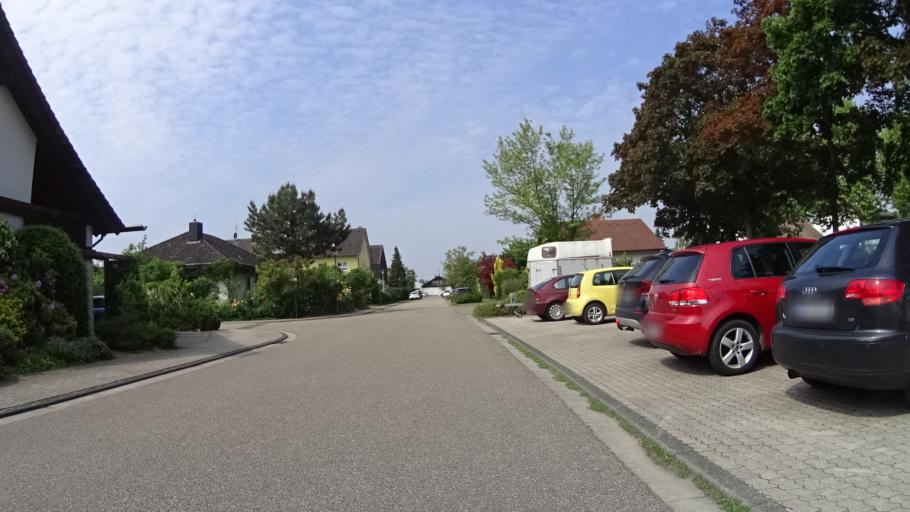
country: DE
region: Baden-Wuerttemberg
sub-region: Karlsruhe Region
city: Graben-Neudorf
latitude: 49.1548
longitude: 8.4748
